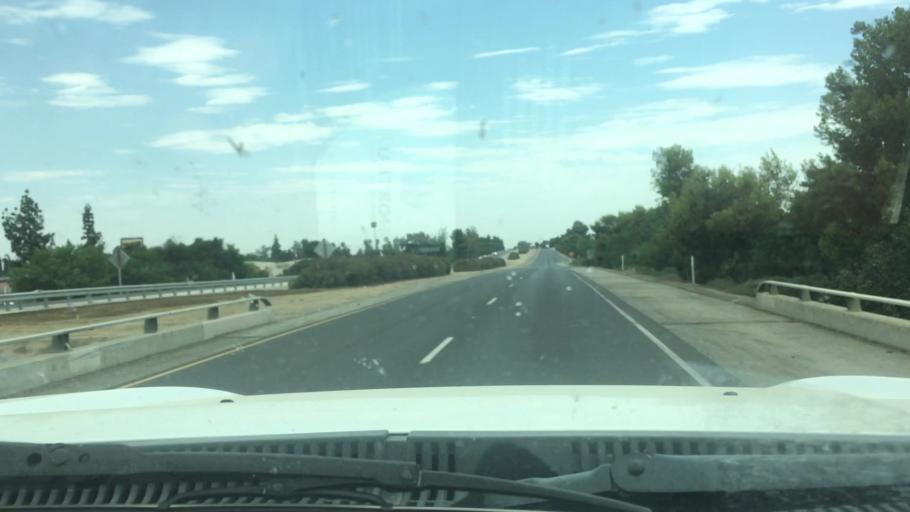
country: US
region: California
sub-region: Tulare County
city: Porterville
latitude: 36.0804
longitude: -119.0395
